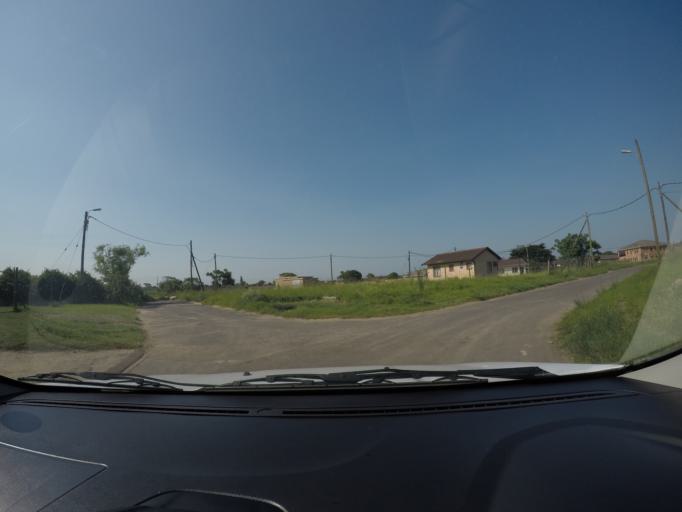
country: ZA
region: KwaZulu-Natal
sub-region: uThungulu District Municipality
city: Richards Bay
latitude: -28.7223
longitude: 32.0351
